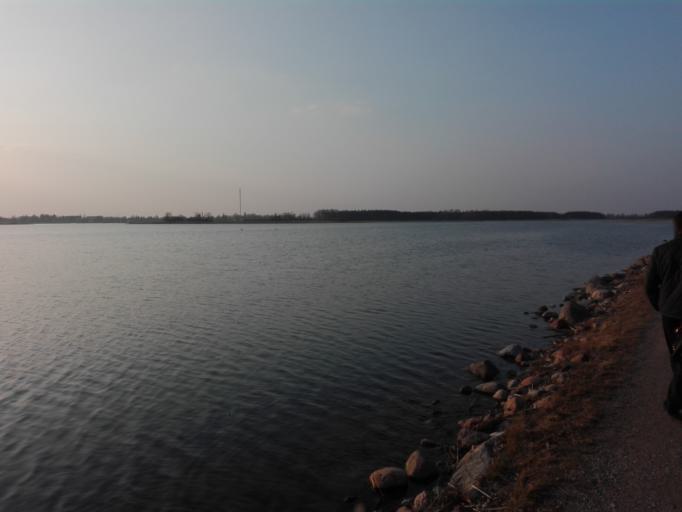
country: LT
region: Panevezys
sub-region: Birzai
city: Birzai
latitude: 56.2061
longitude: 24.7504
